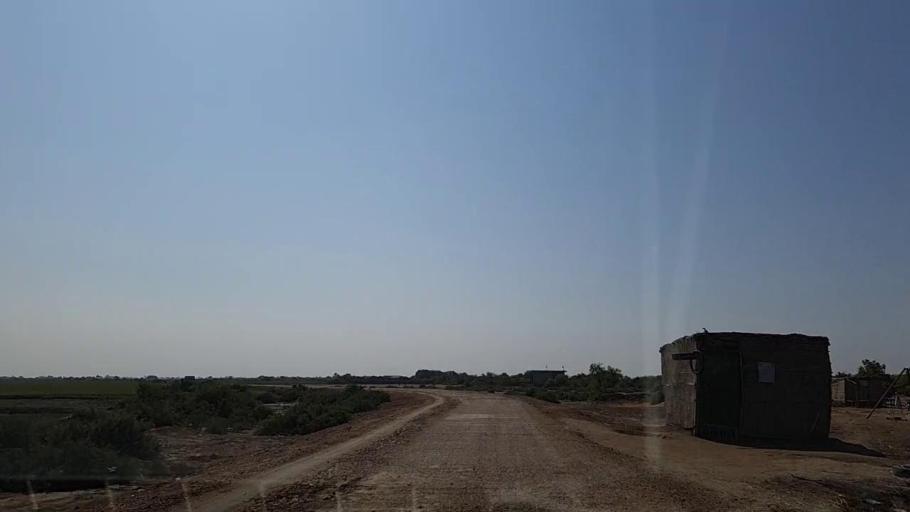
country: PK
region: Sindh
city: Chuhar Jamali
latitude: 24.4745
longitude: 68.0911
